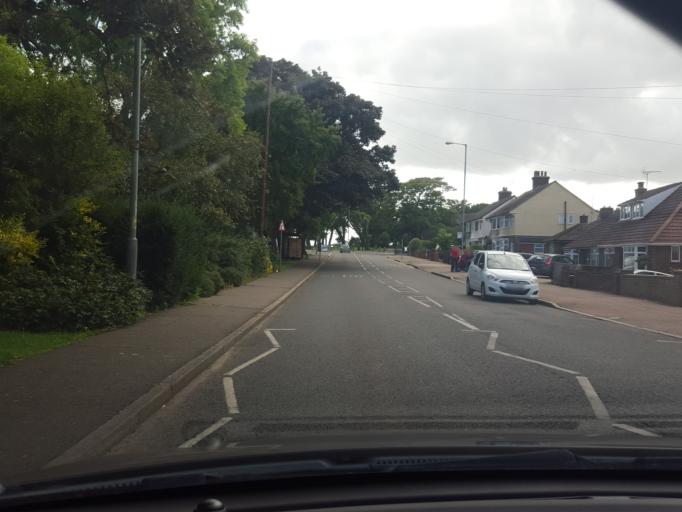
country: GB
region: England
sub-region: Essex
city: Harwich
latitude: 51.9399
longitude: 1.2861
